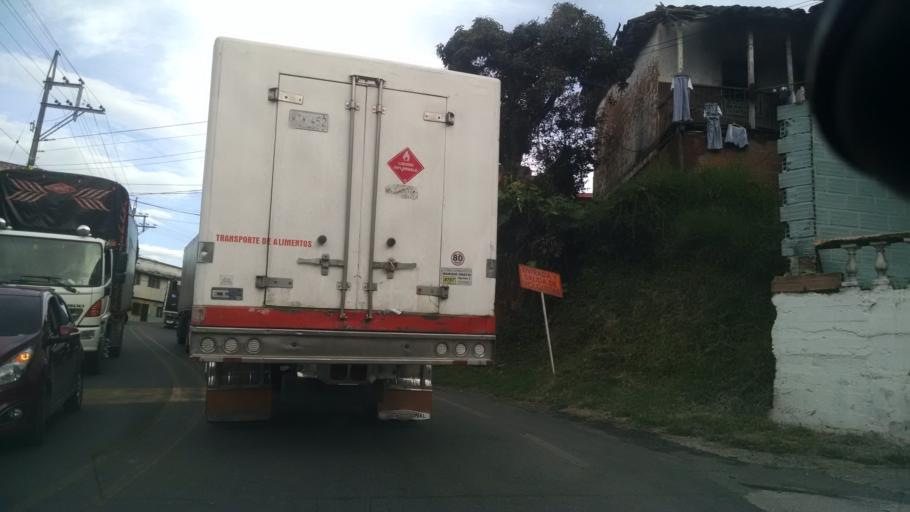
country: CO
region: Antioquia
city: Santa Barbara
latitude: 5.8753
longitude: -75.5663
